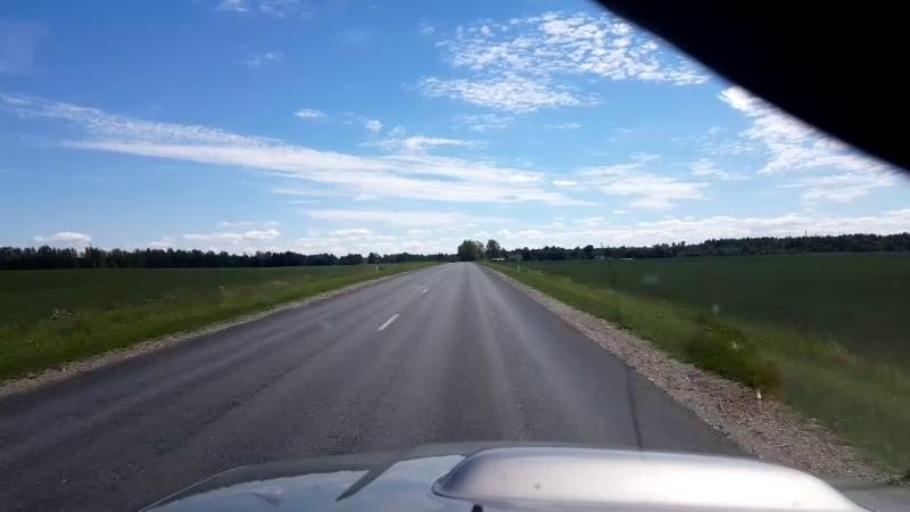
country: EE
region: Laeaene-Virumaa
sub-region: Rakke vald
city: Rakke
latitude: 58.8937
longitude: 26.2844
